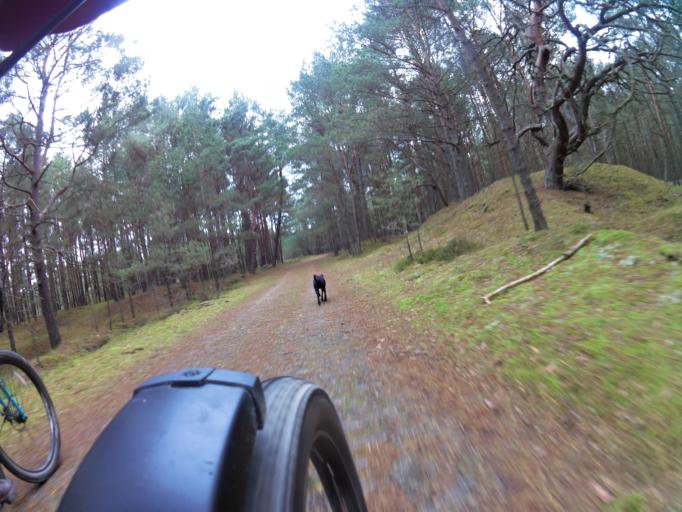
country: PL
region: Pomeranian Voivodeship
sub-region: Powiat leborski
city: Leba
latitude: 54.7691
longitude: 17.5969
